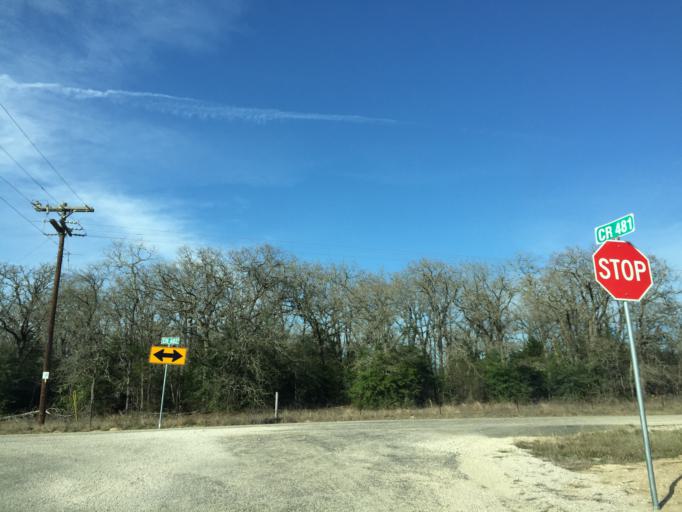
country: US
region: Texas
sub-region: Milam County
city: Thorndale
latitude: 30.4597
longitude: -97.1905
